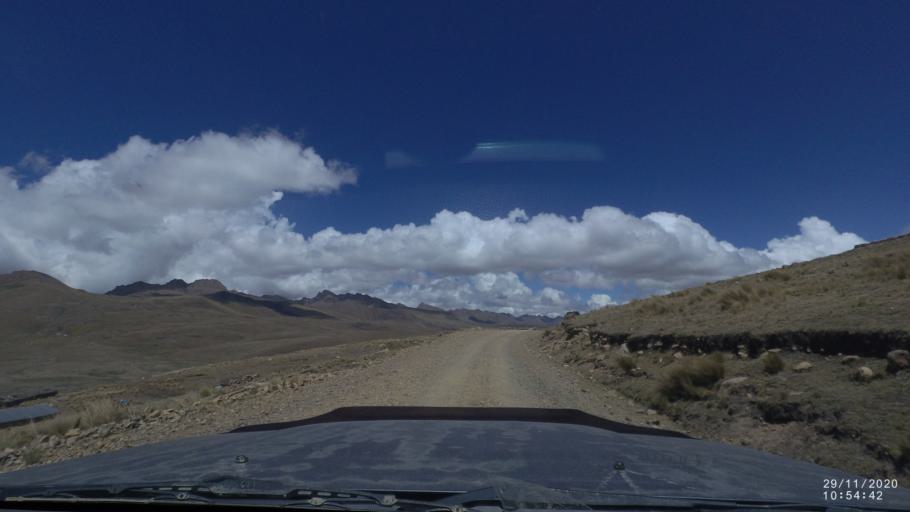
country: BO
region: Cochabamba
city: Cochabamba
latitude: -17.2267
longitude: -66.2210
